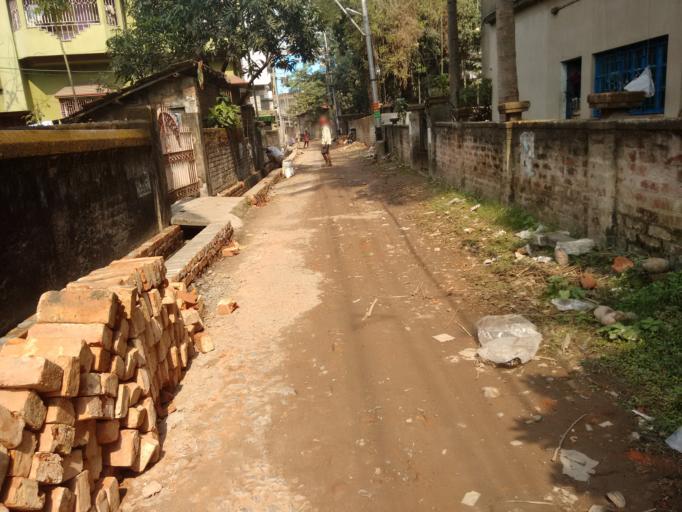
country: IN
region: West Bengal
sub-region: North 24 Parganas
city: Dam Dam
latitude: 22.6493
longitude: 88.4266
